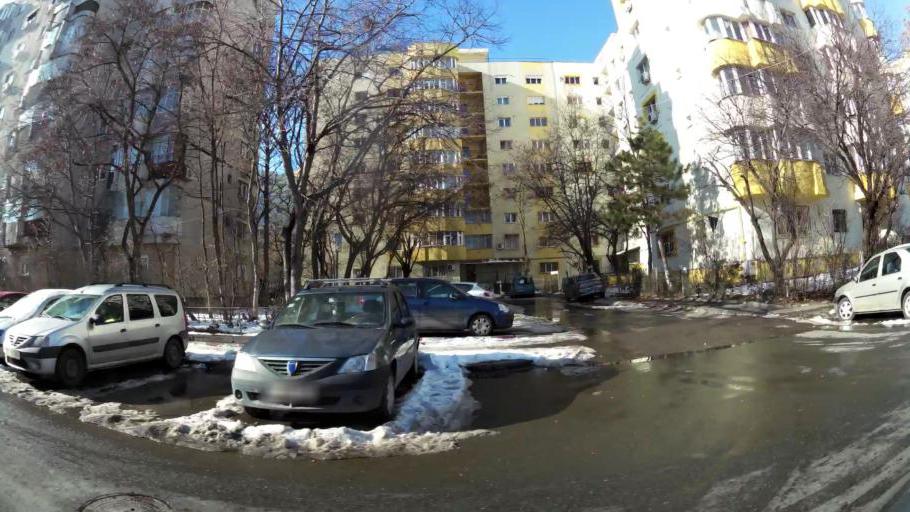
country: RO
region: Bucuresti
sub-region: Municipiul Bucuresti
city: Bucharest
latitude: 44.4576
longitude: 26.1225
